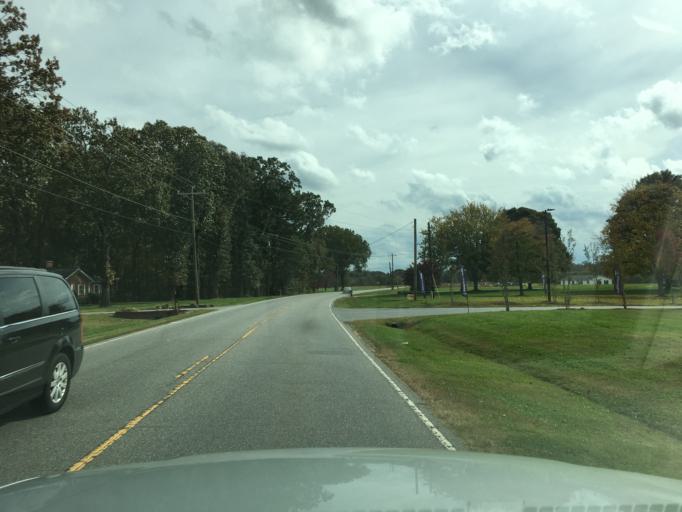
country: US
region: North Carolina
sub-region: Catawba County
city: Newton
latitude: 35.6892
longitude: -81.2808
